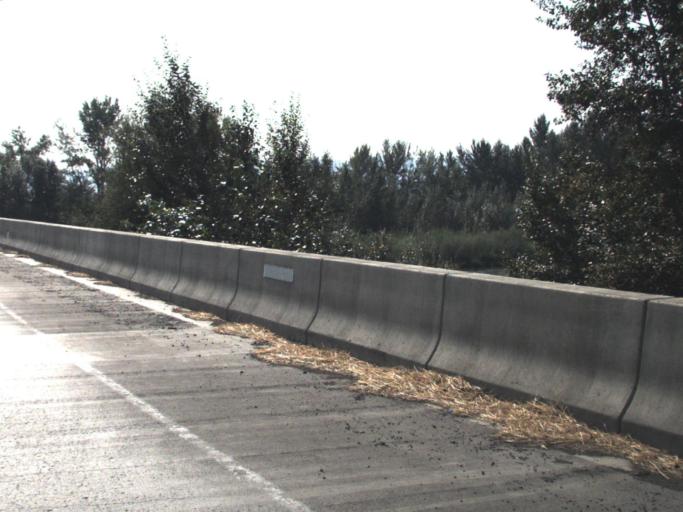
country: US
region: Washington
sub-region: Yakima County
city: Union Gap
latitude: 46.5821
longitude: -120.4630
